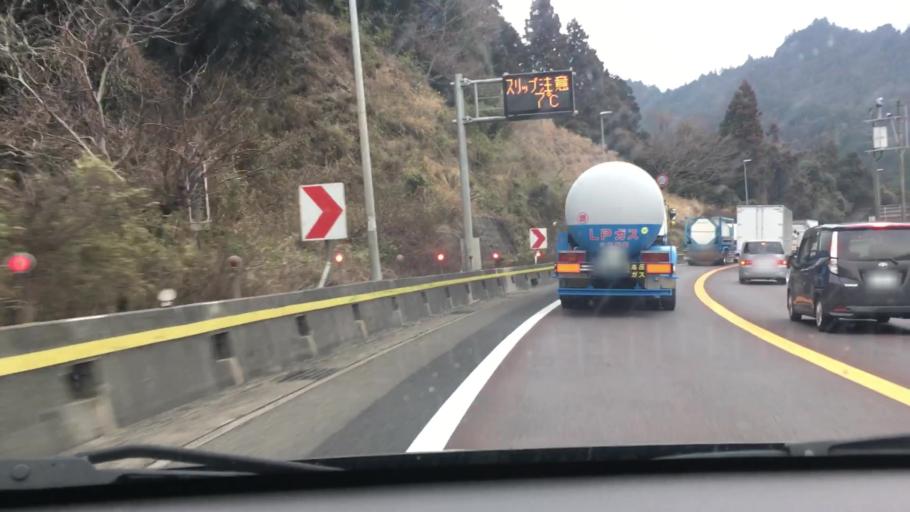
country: JP
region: Mie
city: Kameyama
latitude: 34.8408
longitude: 136.3611
